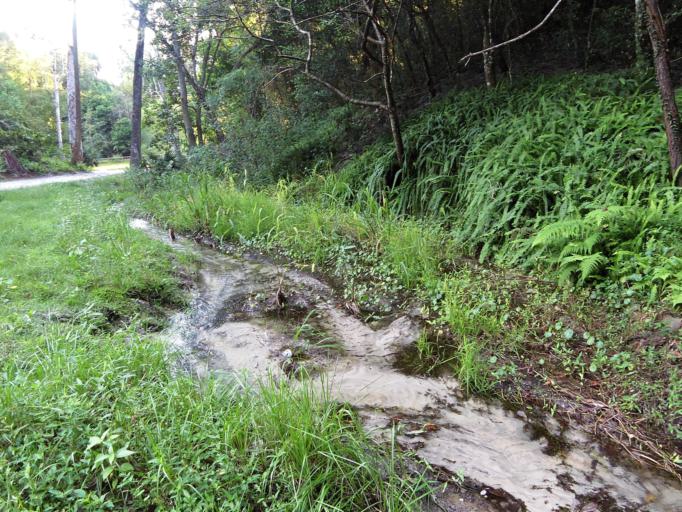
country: US
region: Florida
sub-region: Putnam County
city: Palatka
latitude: 29.6351
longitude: -81.6477
